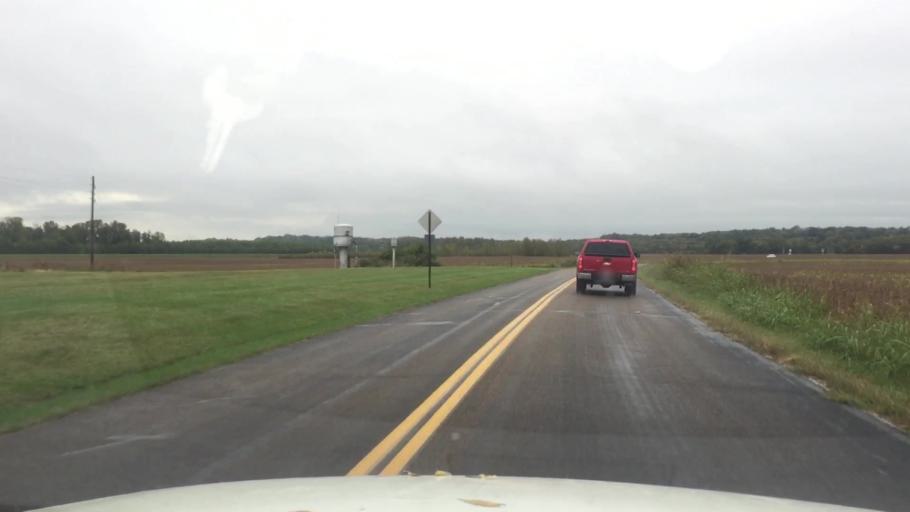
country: US
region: Missouri
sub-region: Boone County
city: Columbia
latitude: 38.8876
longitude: -92.4670
